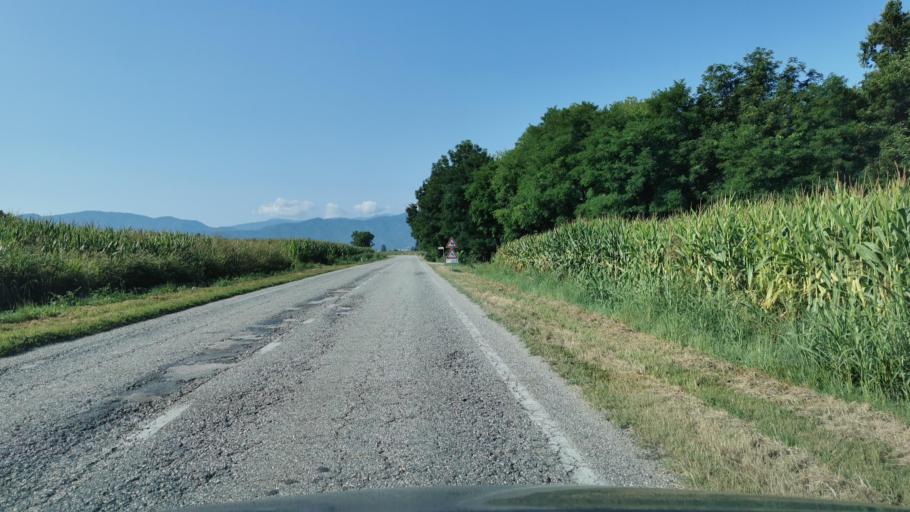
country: IT
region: Piedmont
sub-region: Provincia di Cuneo
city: Carde
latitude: 44.7128
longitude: 7.4379
